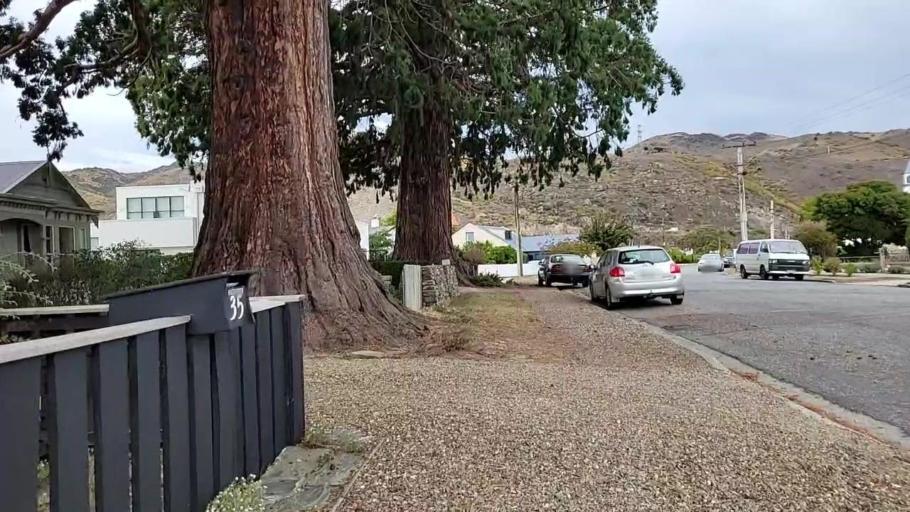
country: NZ
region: Otago
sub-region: Queenstown-Lakes District
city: Wanaka
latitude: -45.0495
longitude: 169.2135
